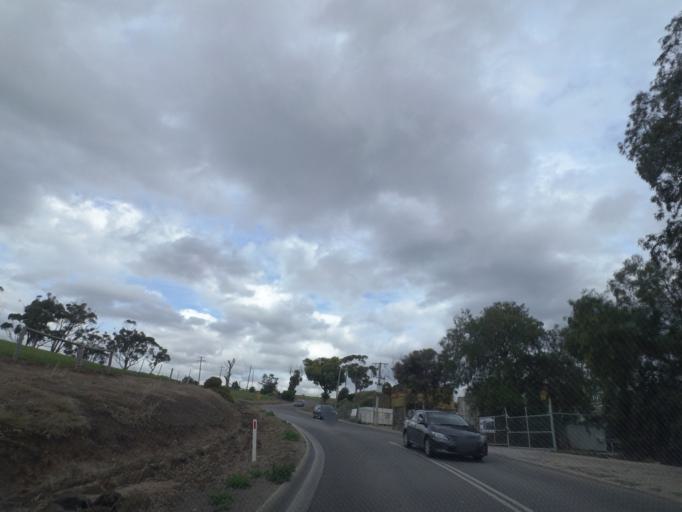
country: AU
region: Victoria
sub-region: Brimbank
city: Keilor
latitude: -37.6998
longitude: 144.8434
